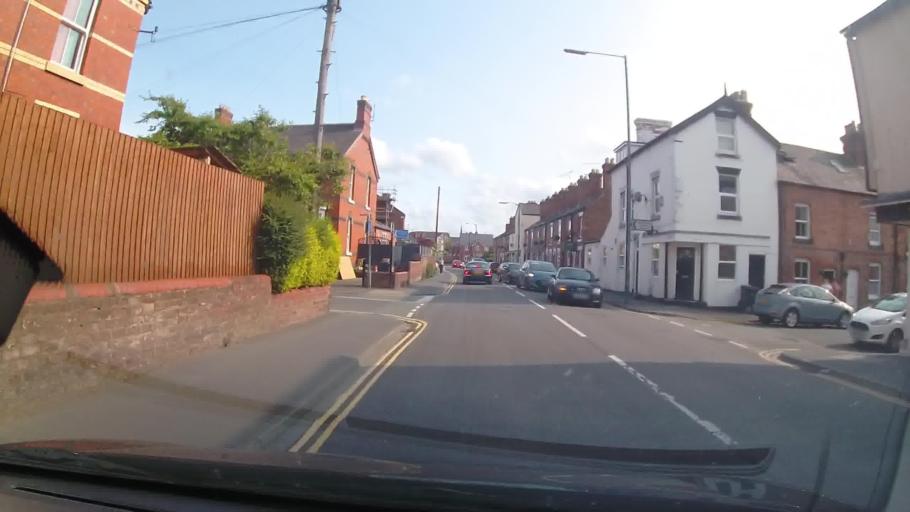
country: GB
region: England
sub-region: Shropshire
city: Shrewsbury
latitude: 52.7200
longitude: -2.7519
